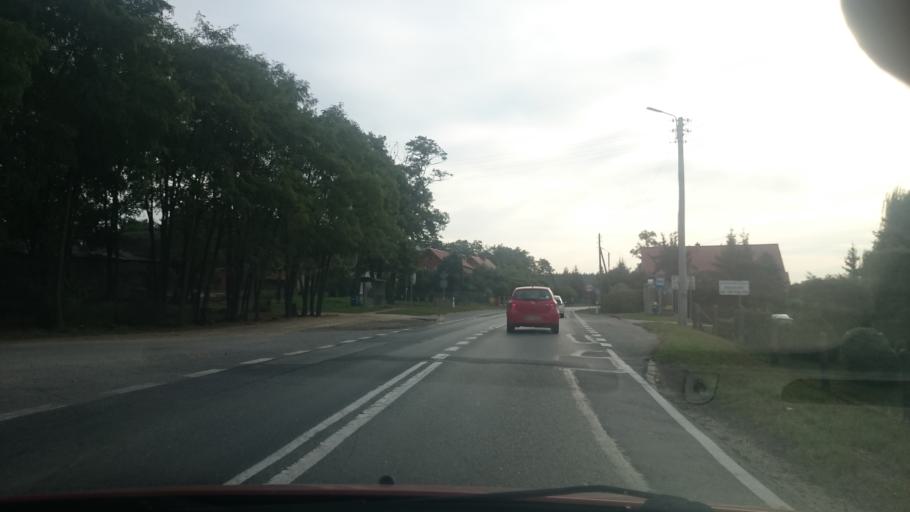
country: PL
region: Lower Silesian Voivodeship
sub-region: Powiat trzebnicki
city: Trzebnica
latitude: 51.3664
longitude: 17.1344
